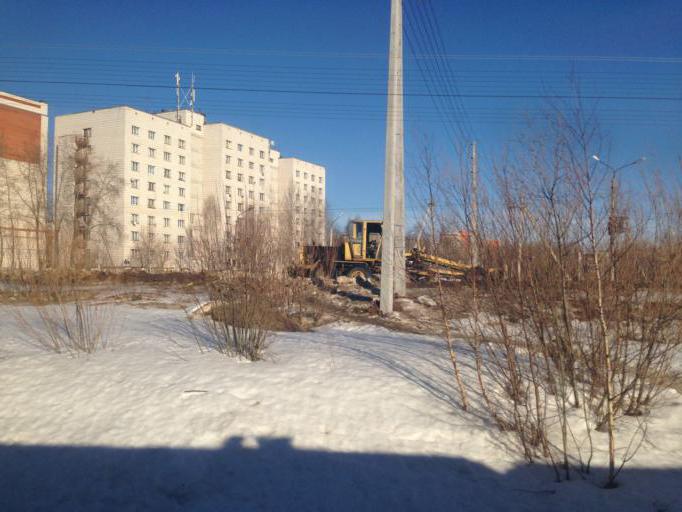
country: RU
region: Komi Republic
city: Ezhva
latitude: 61.7952
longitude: 50.7380
